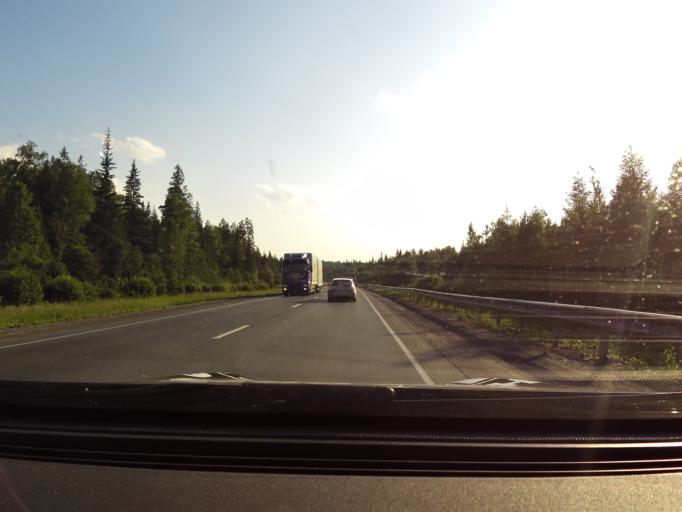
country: RU
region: Sverdlovsk
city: Druzhinino
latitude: 56.8254
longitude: 59.5828
